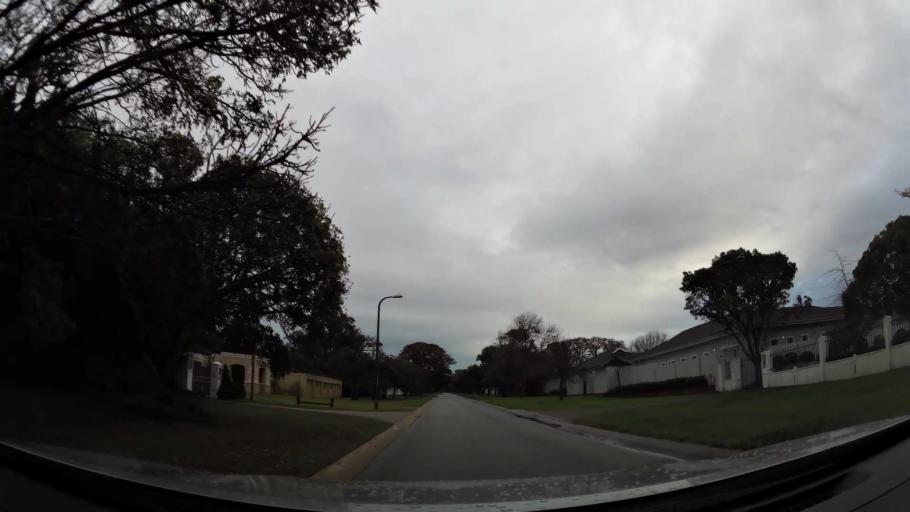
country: ZA
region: Eastern Cape
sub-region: Nelson Mandela Bay Metropolitan Municipality
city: Port Elizabeth
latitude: -33.9793
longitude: 25.5694
